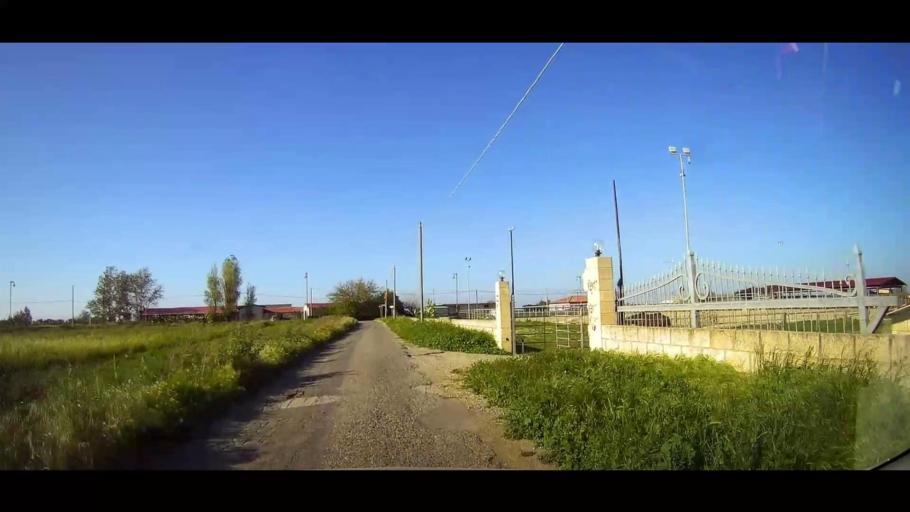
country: IT
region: Calabria
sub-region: Provincia di Crotone
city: Crotone
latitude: 39.0245
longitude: 17.1876
